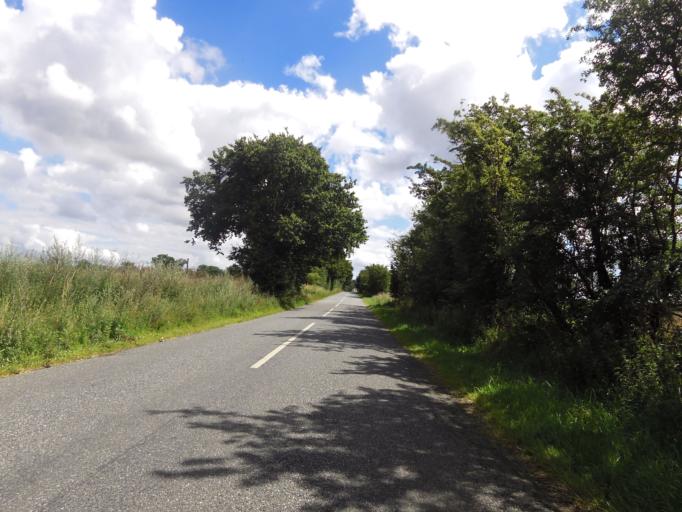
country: DK
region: South Denmark
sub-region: Haderslev Kommune
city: Vojens
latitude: 55.2819
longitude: 9.2349
